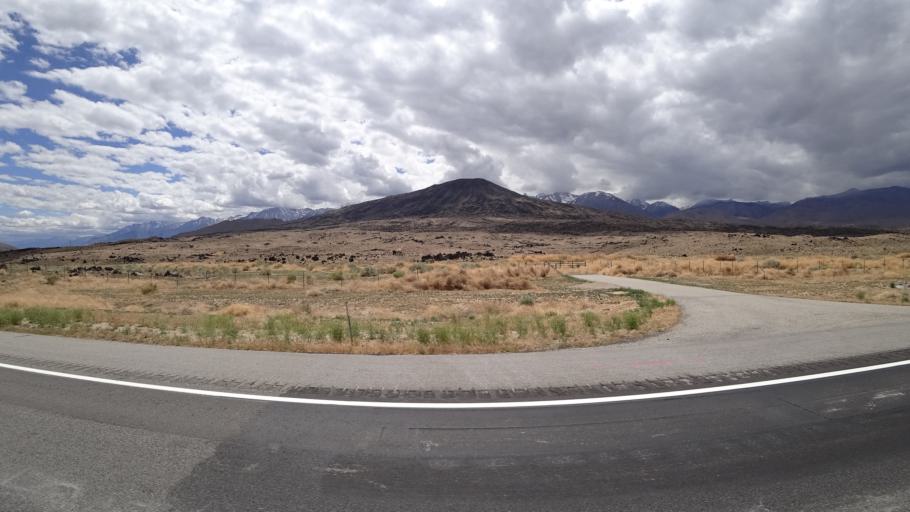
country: US
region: California
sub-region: Inyo County
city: Big Pine
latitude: 37.1278
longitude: -118.2680
